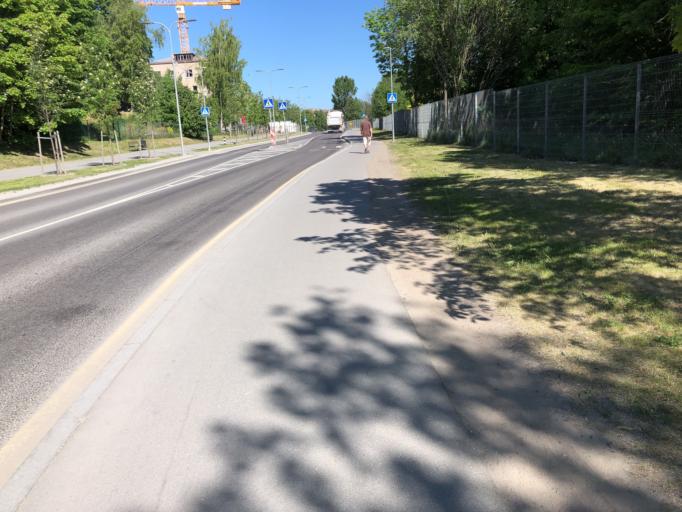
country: EE
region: Harju
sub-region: Tallinna linn
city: Tallinn
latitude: 59.4468
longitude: 24.7463
